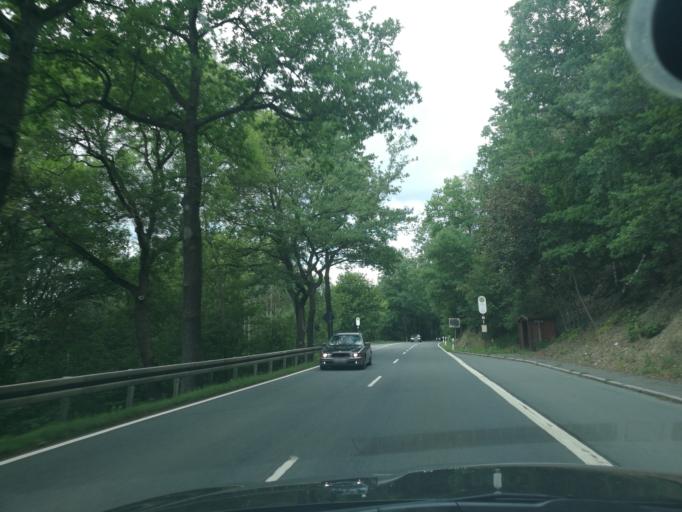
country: DE
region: Saxony
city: Eichigt
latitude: 50.3739
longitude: 12.2072
